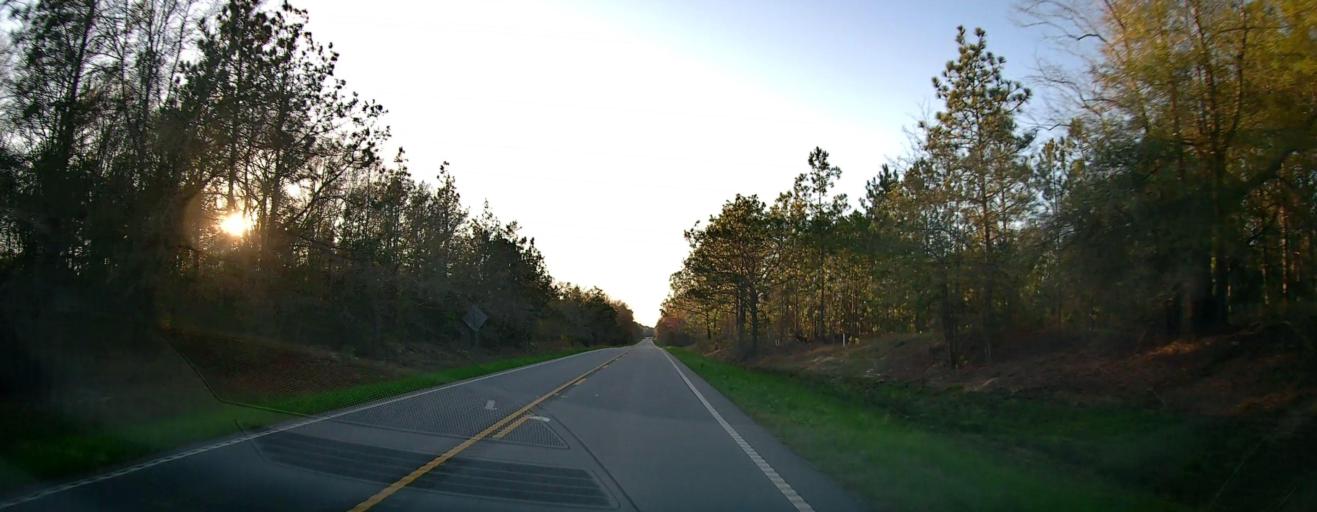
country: US
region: Georgia
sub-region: Wilcox County
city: Rochelle
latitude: 31.9456
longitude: -83.5556
